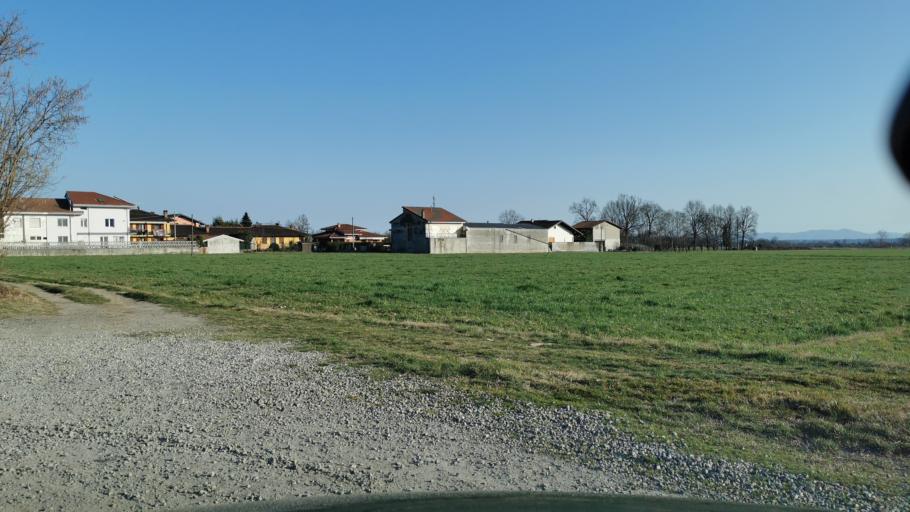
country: IT
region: Piedmont
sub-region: Provincia di Torino
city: Favria
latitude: 45.3283
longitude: 7.6837
